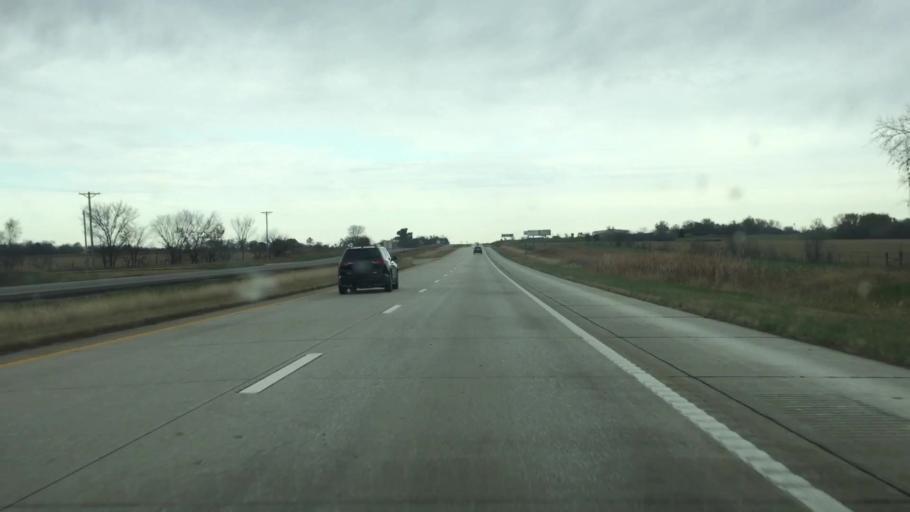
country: US
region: Missouri
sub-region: Saint Clair County
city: Osceola
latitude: 38.1576
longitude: -93.7224
